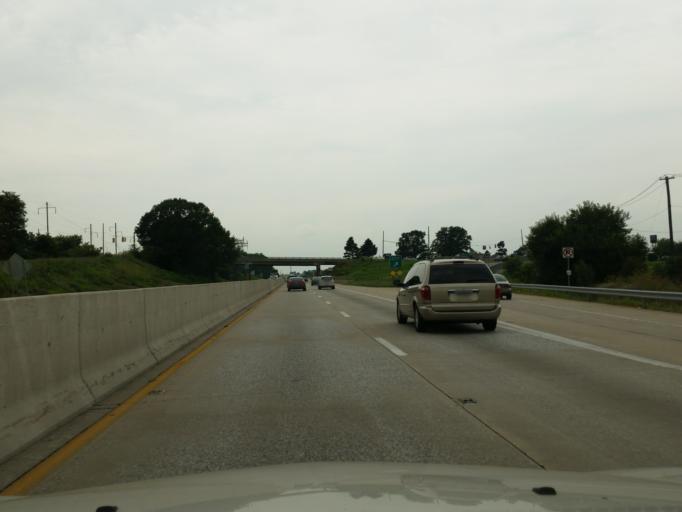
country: US
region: Pennsylvania
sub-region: Lancaster County
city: East Petersburg
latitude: 40.0878
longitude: -76.3783
